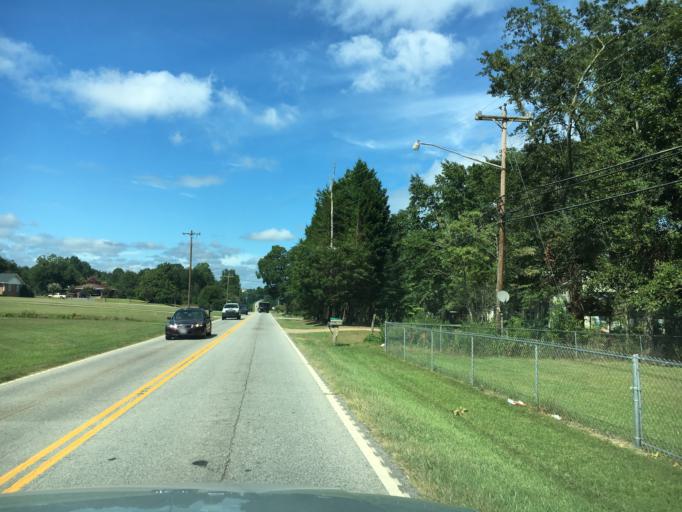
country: US
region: South Carolina
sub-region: Spartanburg County
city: Lyman
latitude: 34.9678
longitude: -82.1211
